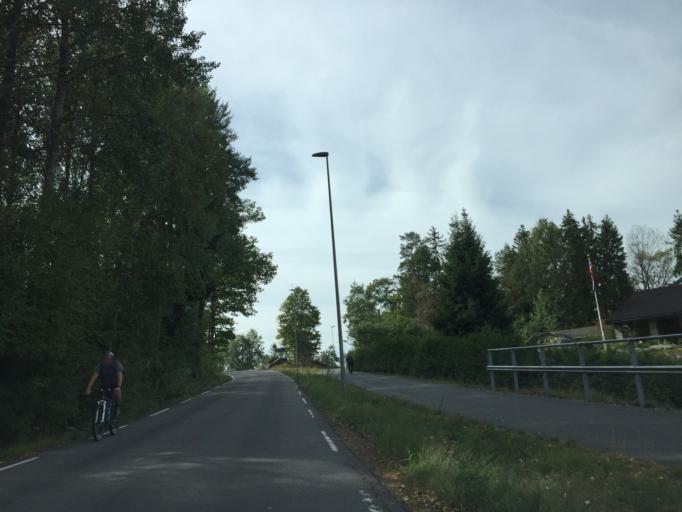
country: NO
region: Ostfold
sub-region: Moss
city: Moss
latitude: 59.4908
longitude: 10.6914
